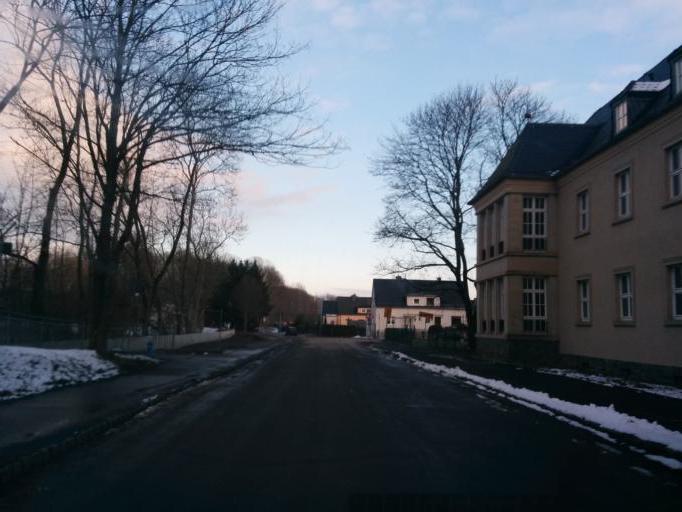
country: DE
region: Saxony
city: Floha
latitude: 50.8588
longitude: 13.0795
